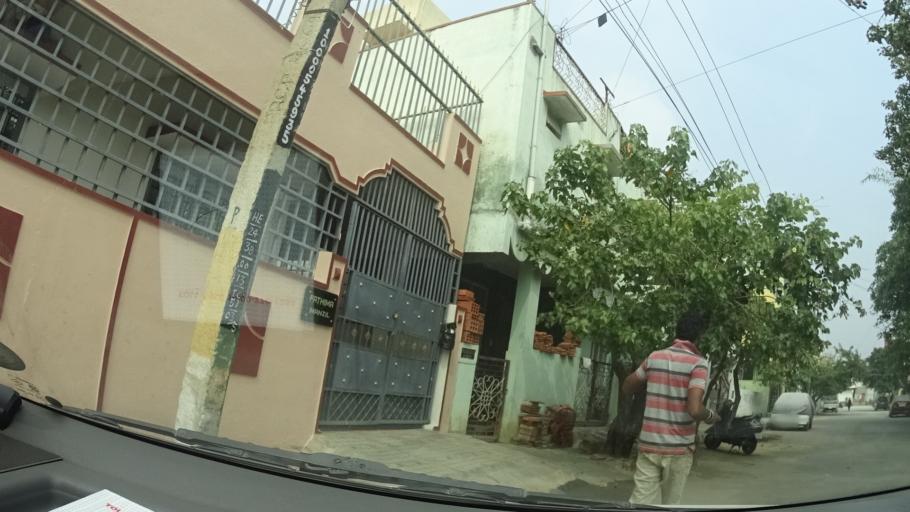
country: IN
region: Karnataka
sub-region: Bangalore Urban
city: Bangalore
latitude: 13.0283
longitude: 77.6240
